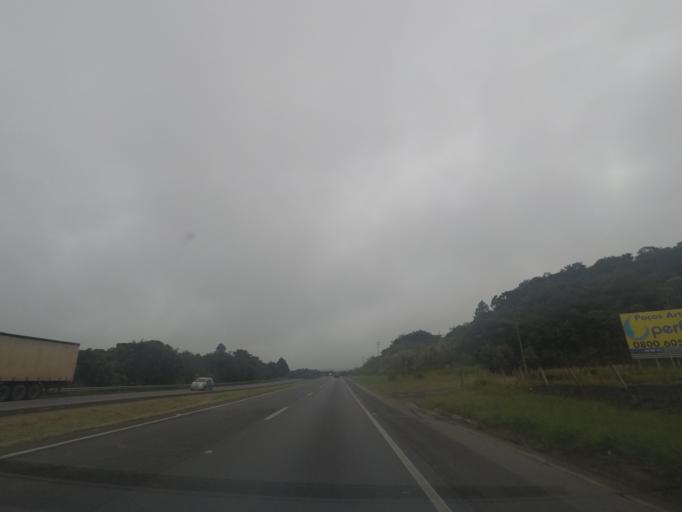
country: BR
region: Parana
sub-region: Campina Grande Do Sul
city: Campina Grande do Sul
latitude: -25.2594
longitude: -48.9139
